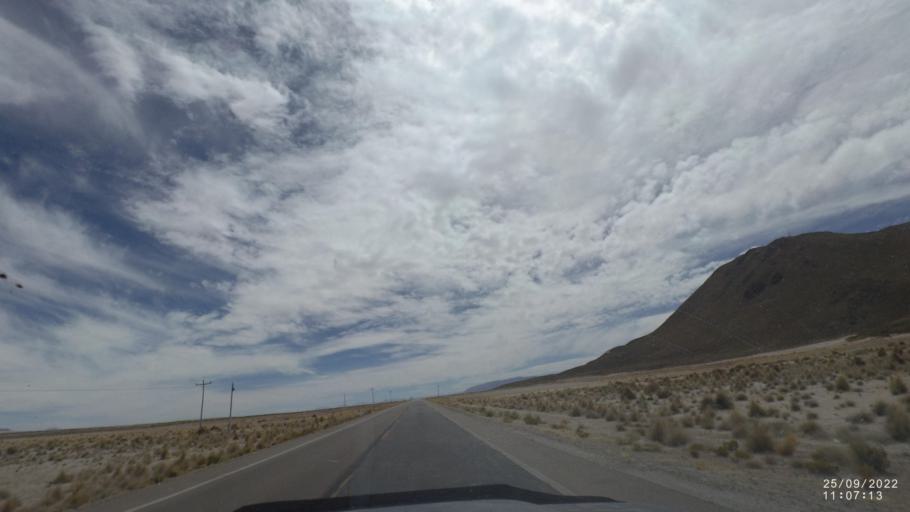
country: BO
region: Oruro
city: Challapata
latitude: -19.3478
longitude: -66.8551
